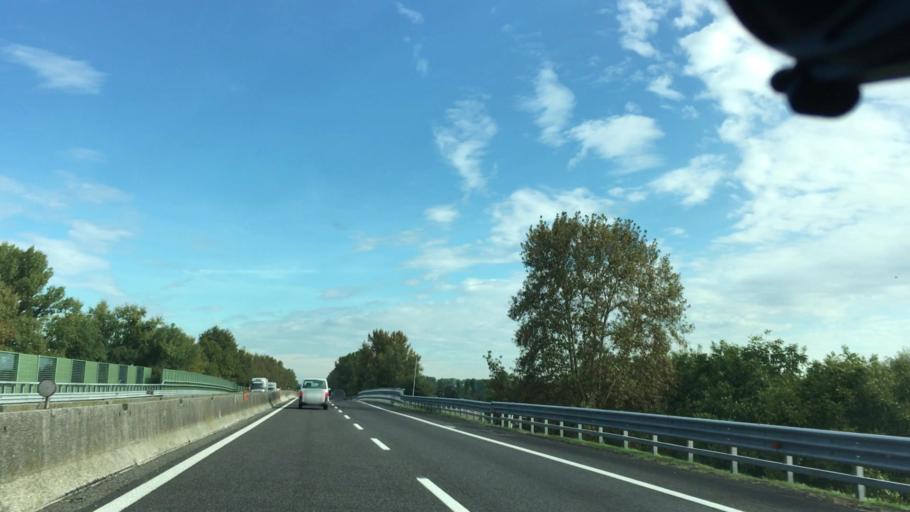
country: IT
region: Emilia-Romagna
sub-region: Provincia di Ferrara
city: Porotto-Cassama
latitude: 44.8427
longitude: 11.5644
